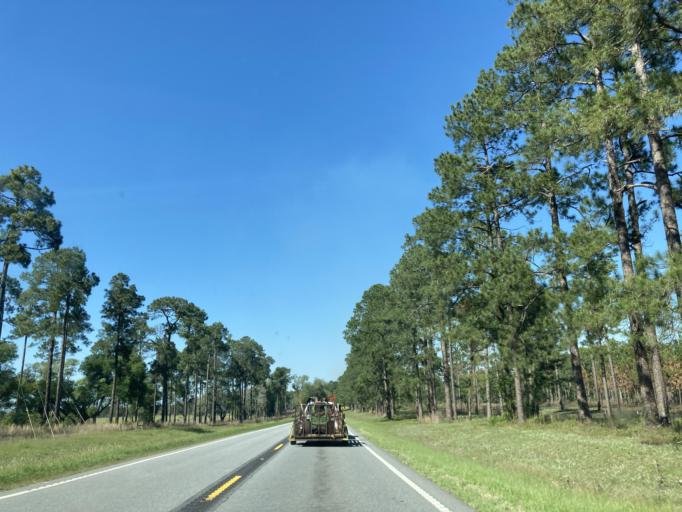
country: US
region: Georgia
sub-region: Baker County
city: Newton
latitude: 31.3913
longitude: -84.2794
